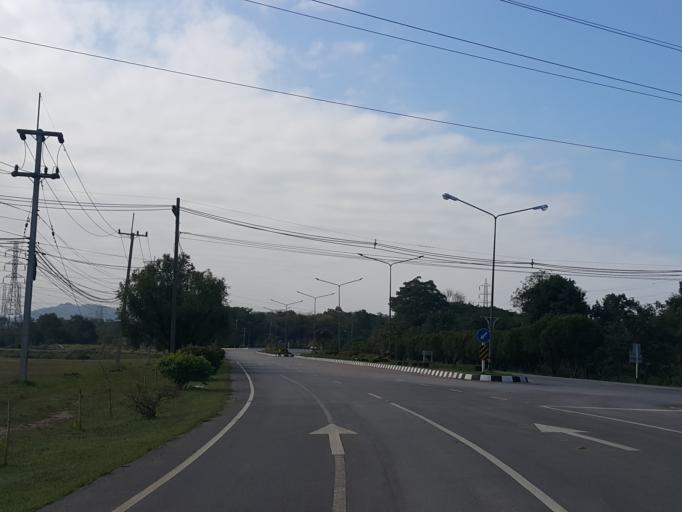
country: TH
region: Lampang
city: Mae Mo
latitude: 18.2993
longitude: 99.7414
